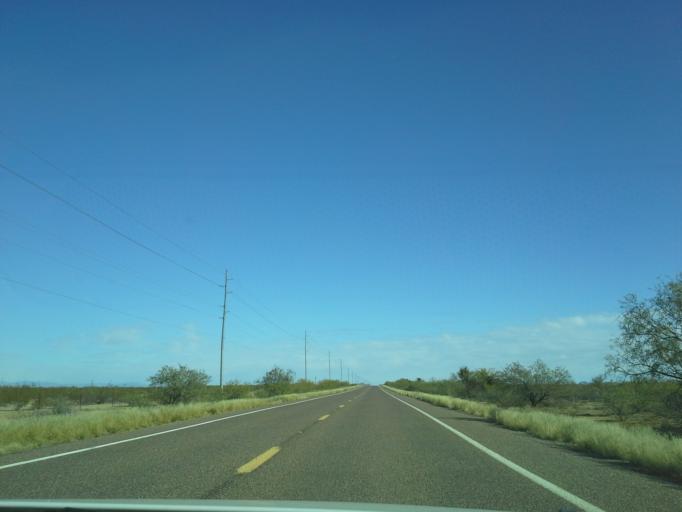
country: US
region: Arizona
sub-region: Yavapai County
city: Congress
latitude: 33.9430
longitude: -113.0479
